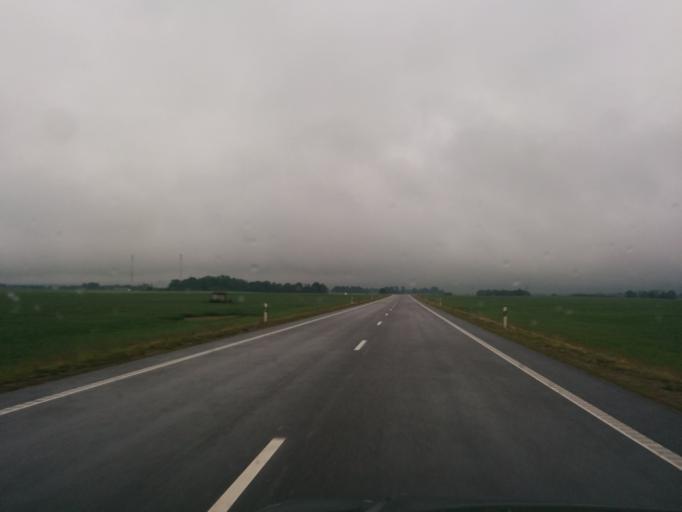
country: LT
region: Panevezys
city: Pasvalys
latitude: 56.2097
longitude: 24.4261
